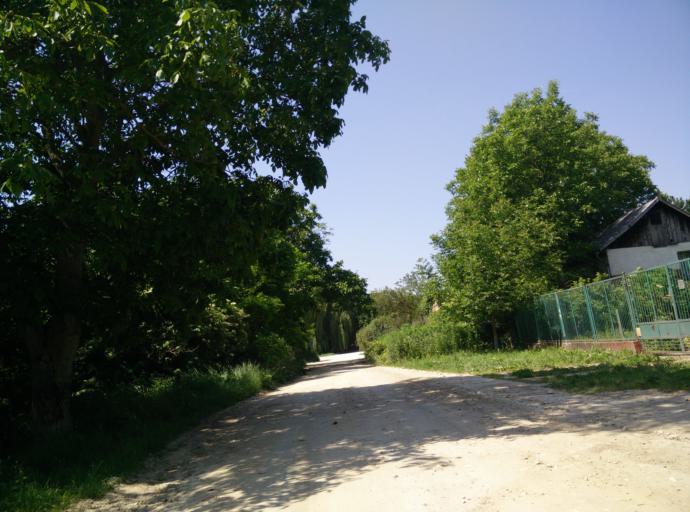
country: HU
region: Pest
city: Biatorbagy
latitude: 47.4670
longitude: 18.8279
